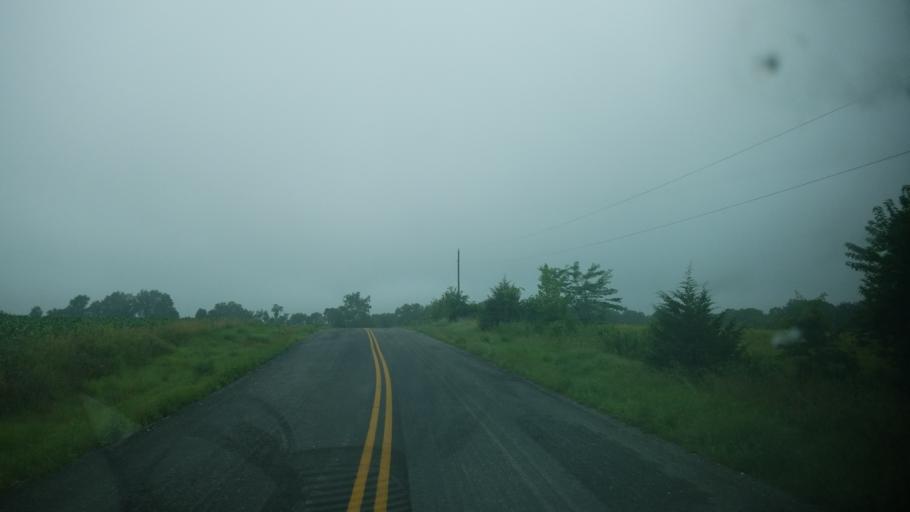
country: US
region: Missouri
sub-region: Audrain County
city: Vandalia
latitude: 39.2876
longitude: -91.3470
